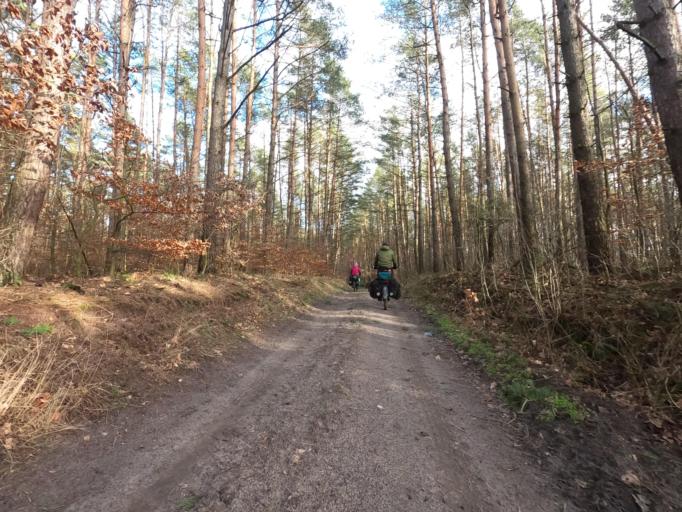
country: PL
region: Greater Poland Voivodeship
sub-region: Powiat pilski
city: Miasteczko Krajenskie
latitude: 53.1026
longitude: 17.0632
